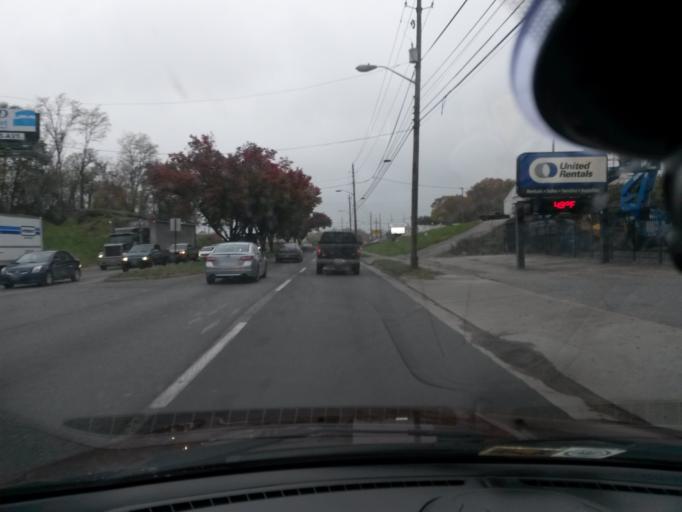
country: US
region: Virginia
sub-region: Roanoke County
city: Vinton
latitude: 37.2840
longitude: -79.9201
